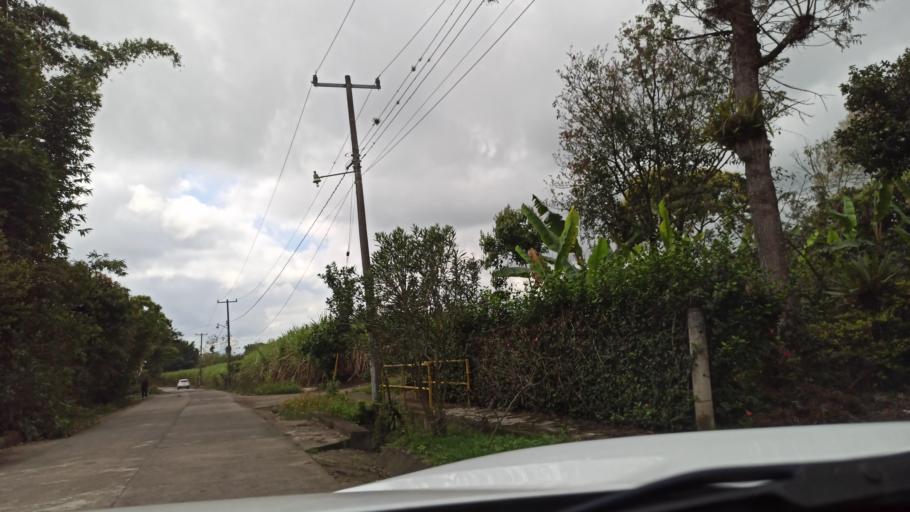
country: MX
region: Veracruz
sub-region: Chocaman
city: San Jose Neria
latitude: 19.0070
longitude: -97.0042
